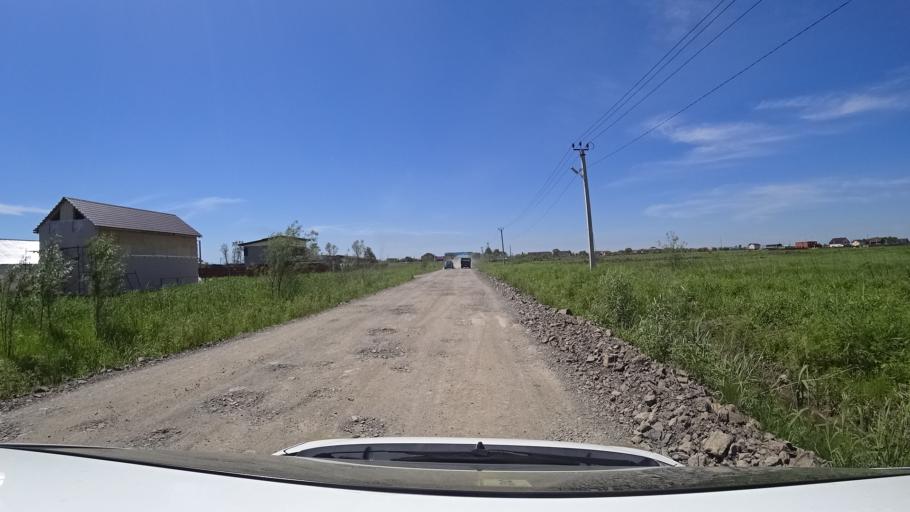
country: RU
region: Khabarovsk Krai
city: Topolevo
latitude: 48.5136
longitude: 135.1917
